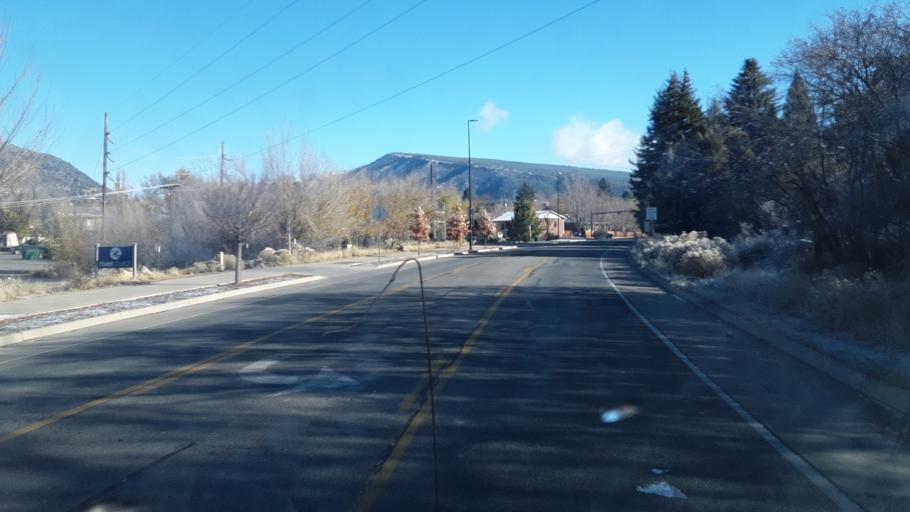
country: US
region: Colorado
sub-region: La Plata County
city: Durango
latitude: 37.2914
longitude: -107.8624
